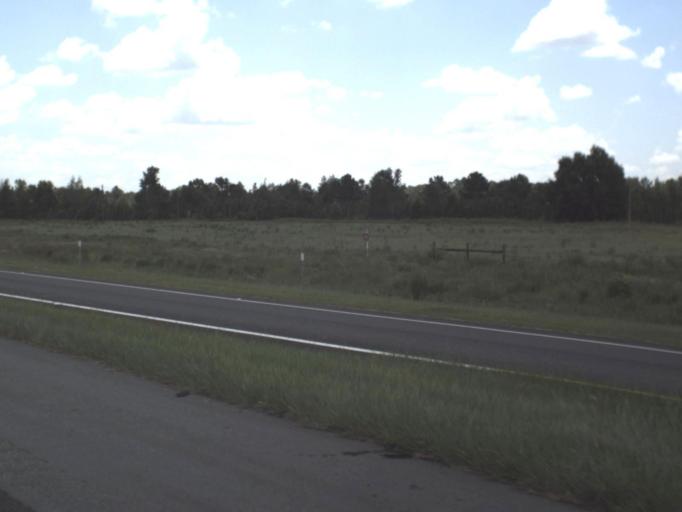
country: US
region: Florida
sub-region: Madison County
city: Madison
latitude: 30.3789
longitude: -83.2944
